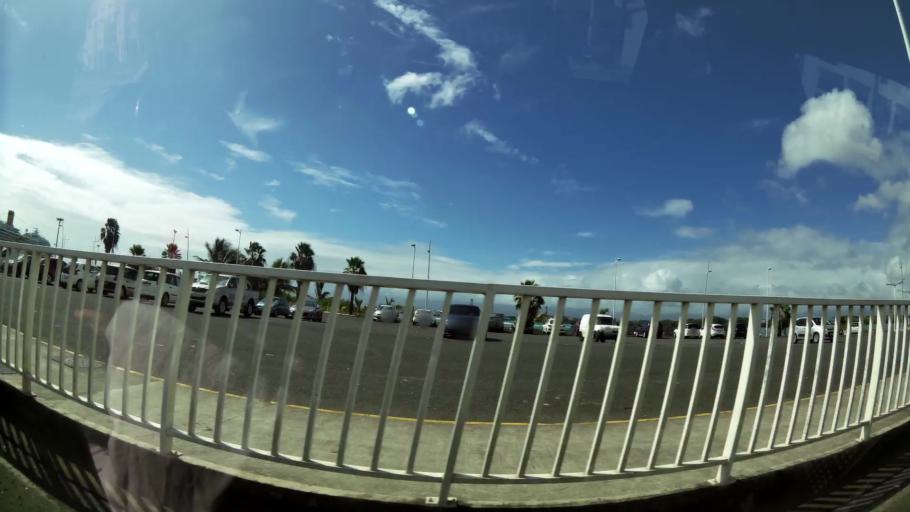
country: GP
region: Guadeloupe
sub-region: Guadeloupe
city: Pointe-a-Pitre
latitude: 16.2439
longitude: -61.5409
